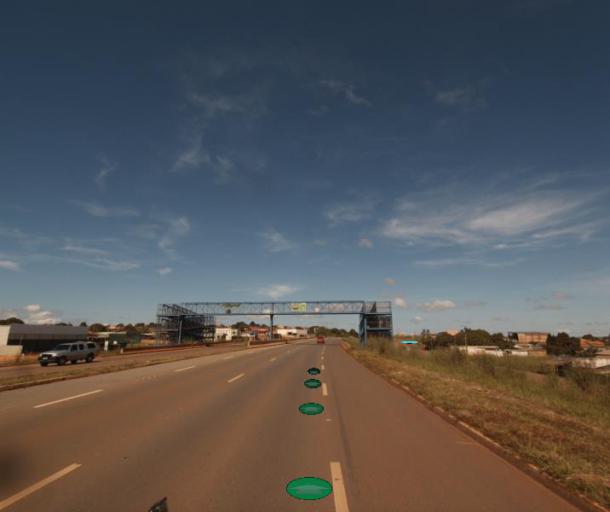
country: BR
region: Federal District
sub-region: Brasilia
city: Brasilia
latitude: -15.7527
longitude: -48.3267
